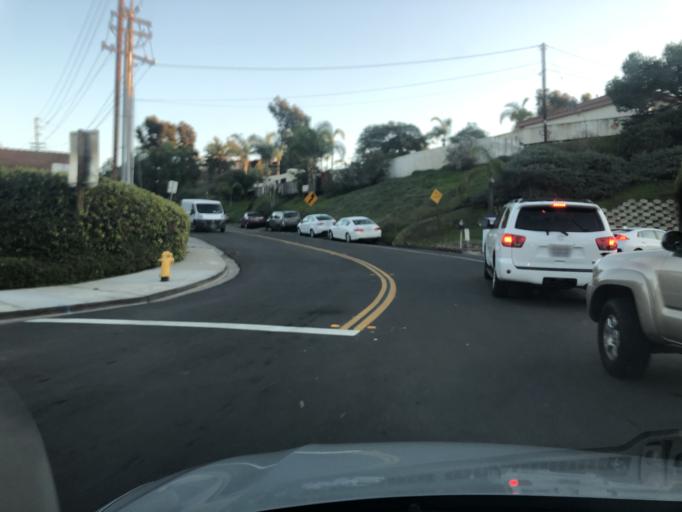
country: US
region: California
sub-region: San Diego County
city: Chula Vista
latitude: 32.6478
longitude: -117.0579
